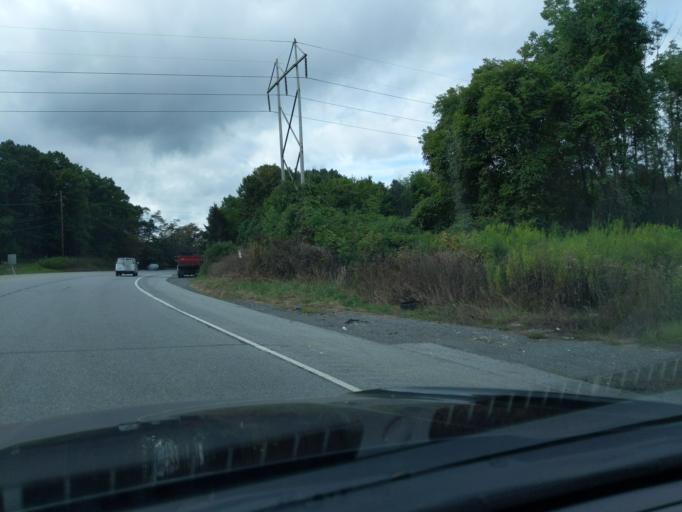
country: US
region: Pennsylvania
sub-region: Blair County
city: Hollidaysburg
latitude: 40.4117
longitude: -78.3987
